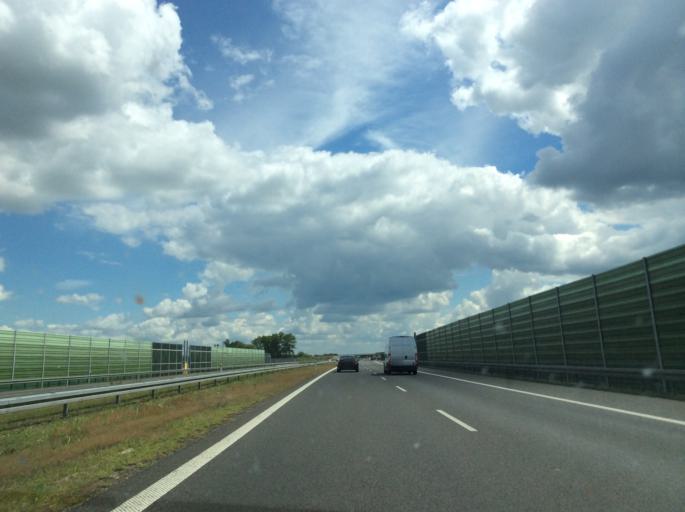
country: PL
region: Greater Poland Voivodeship
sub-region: Powiat kolski
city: Dabie
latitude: 52.1110
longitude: 18.7417
